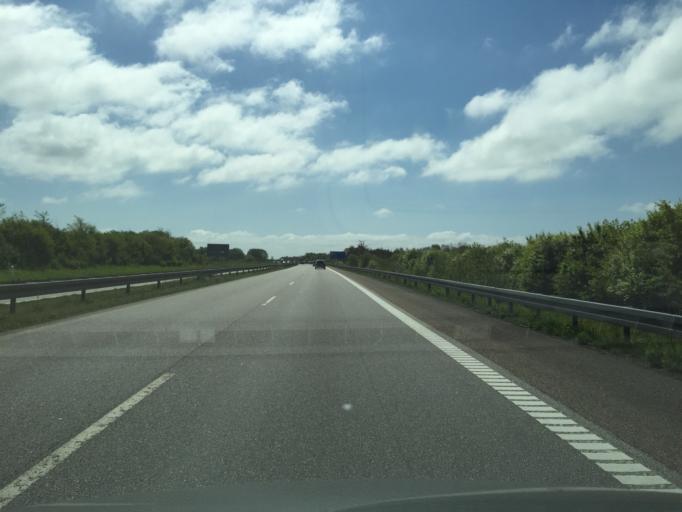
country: DK
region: Zealand
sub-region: Vordingborg Kommune
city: Nyrad
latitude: 55.0109
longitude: 11.9866
